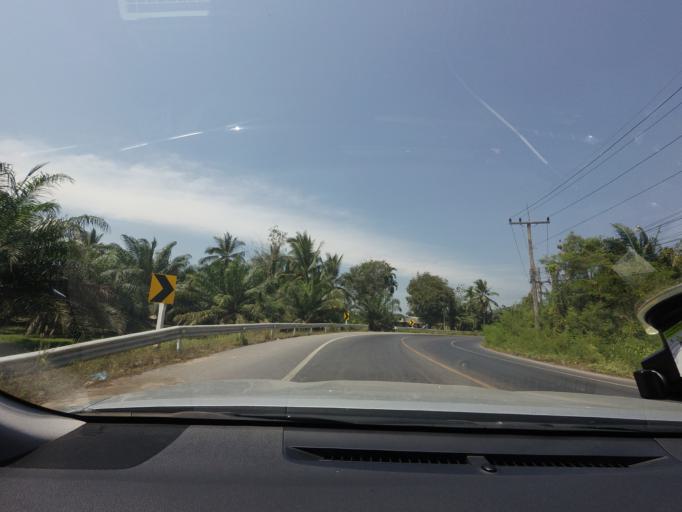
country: TH
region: Surat Thani
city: Phunphin
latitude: 9.1921
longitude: 99.2497
